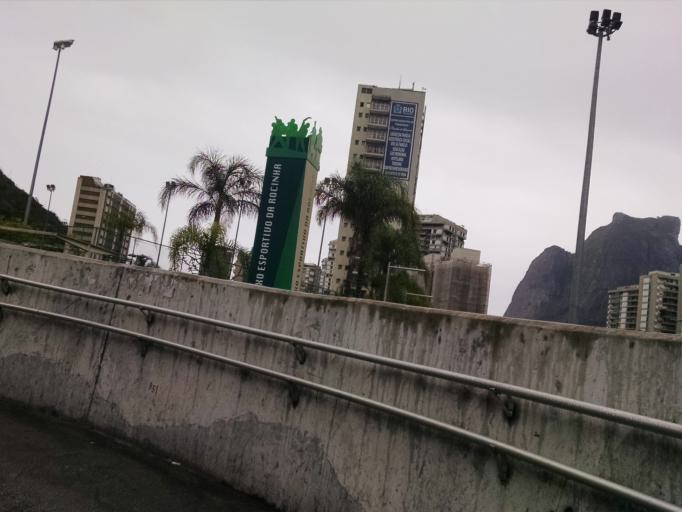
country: BR
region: Rio de Janeiro
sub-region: Rio De Janeiro
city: Rio de Janeiro
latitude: -22.9926
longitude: -43.2514
